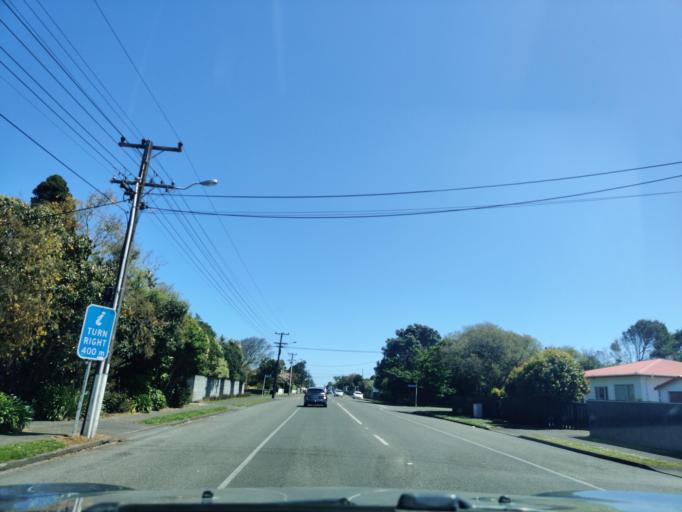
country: NZ
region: Taranaki
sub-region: South Taranaki District
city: Hawera
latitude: -39.5957
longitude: 174.2886
